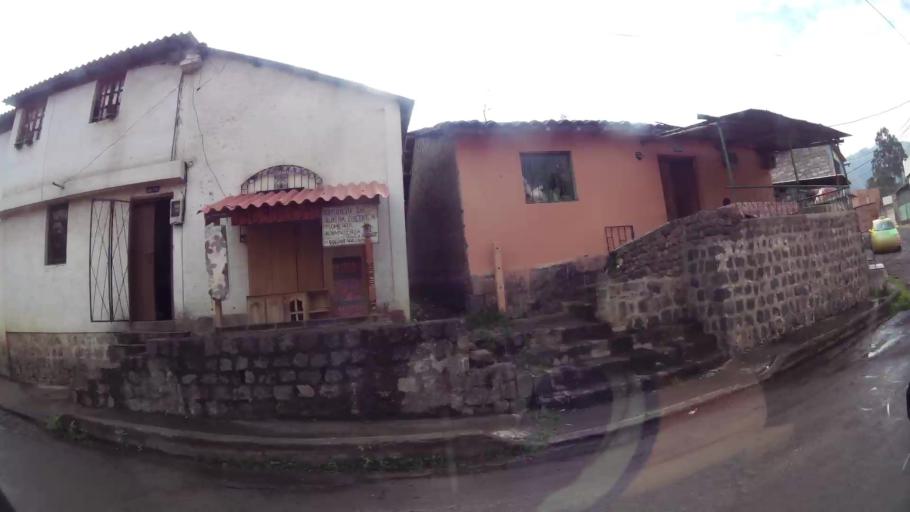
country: EC
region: Pichincha
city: Sangolqui
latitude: -0.3041
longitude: -78.4313
